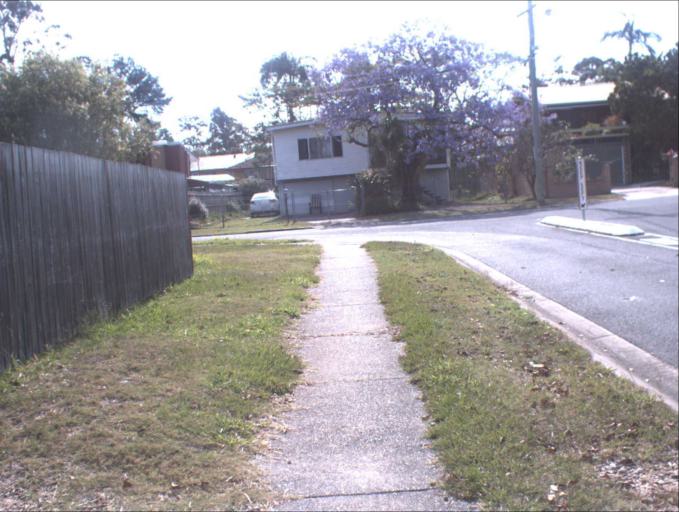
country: AU
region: Queensland
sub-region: Logan
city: Woodridge
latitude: -27.6337
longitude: 153.1010
